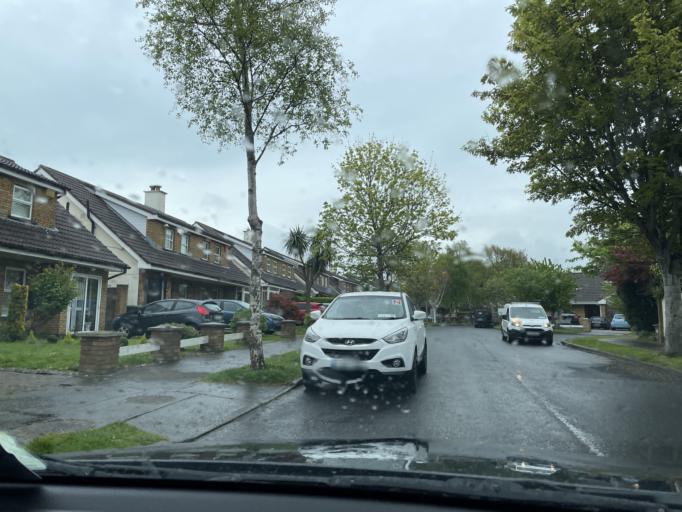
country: IE
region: Leinster
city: Dundrum
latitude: 53.2861
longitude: -6.2725
